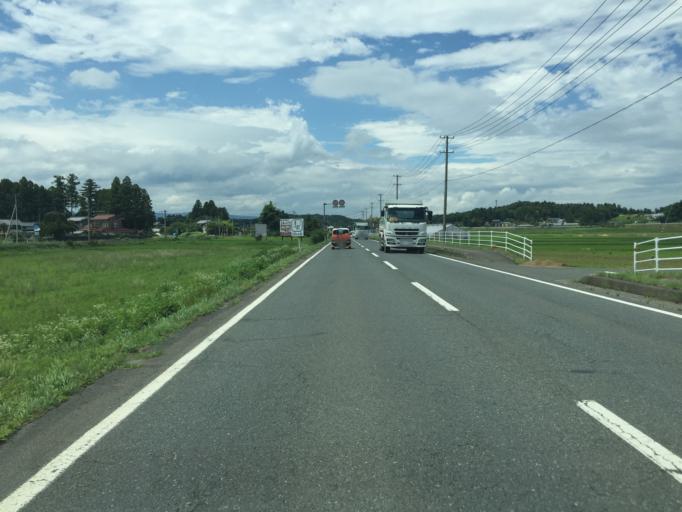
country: JP
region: Fukushima
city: Namie
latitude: 37.7144
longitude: 140.9609
